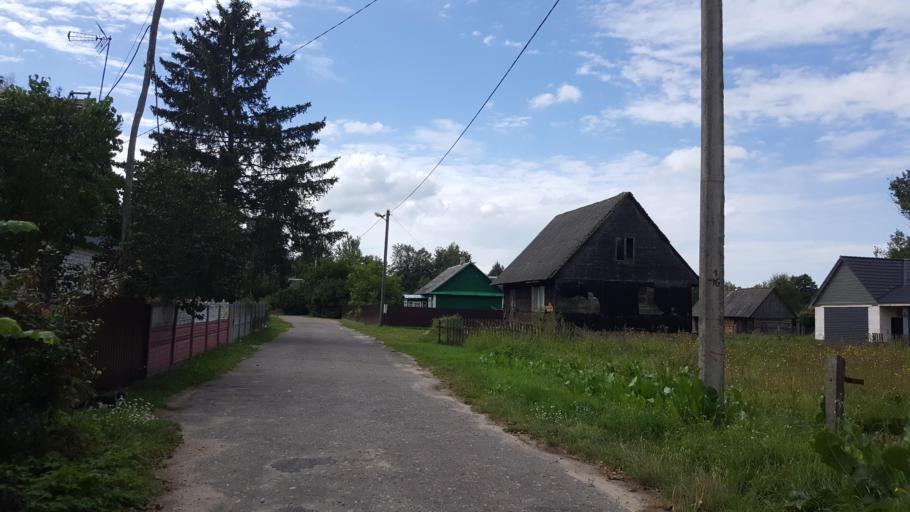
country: BY
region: Brest
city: Zhabinka
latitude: 52.2547
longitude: 23.9645
